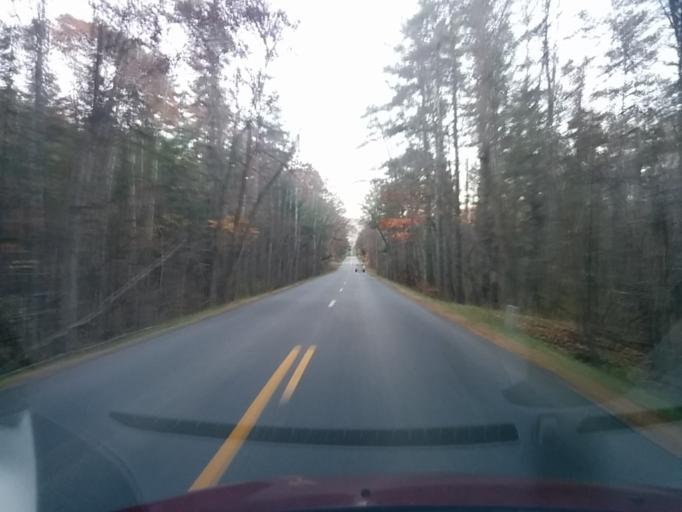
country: US
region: Virginia
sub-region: City of Lexington
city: Lexington
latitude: 37.9203
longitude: -79.5838
